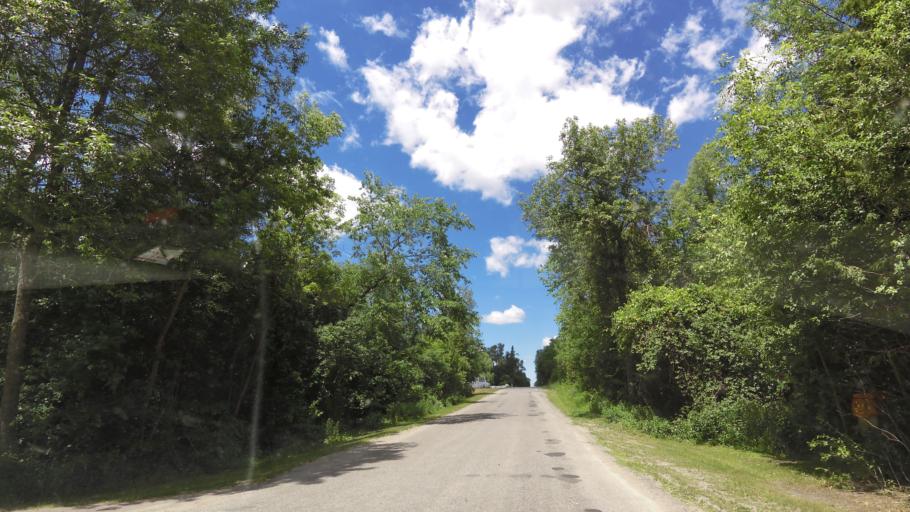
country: CA
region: Ontario
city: Oshawa
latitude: 43.9750
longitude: -78.6274
